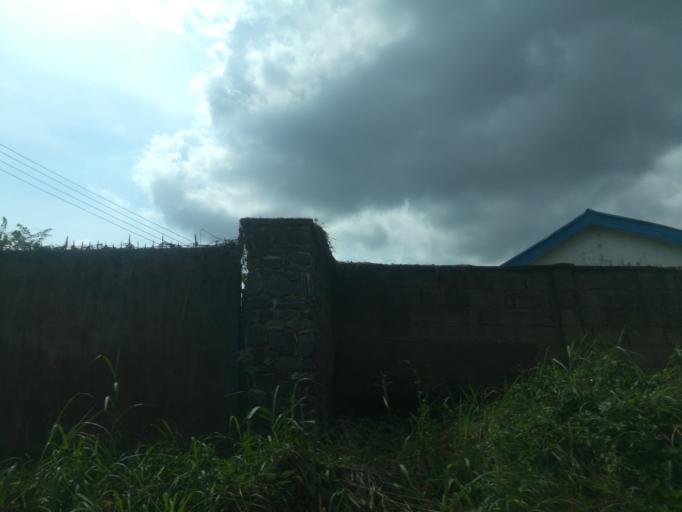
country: NG
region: Oyo
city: Ibadan
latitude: 7.3785
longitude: 3.8360
